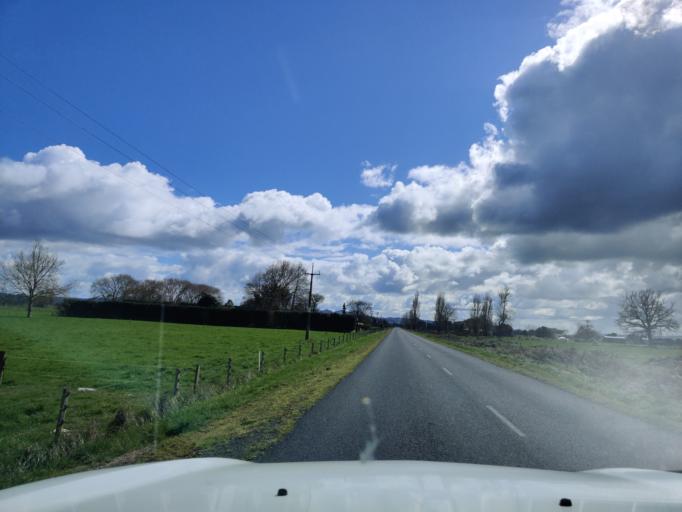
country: NZ
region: Waikato
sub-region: Waikato District
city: Ngaruawahia
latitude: -37.6008
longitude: 175.3003
